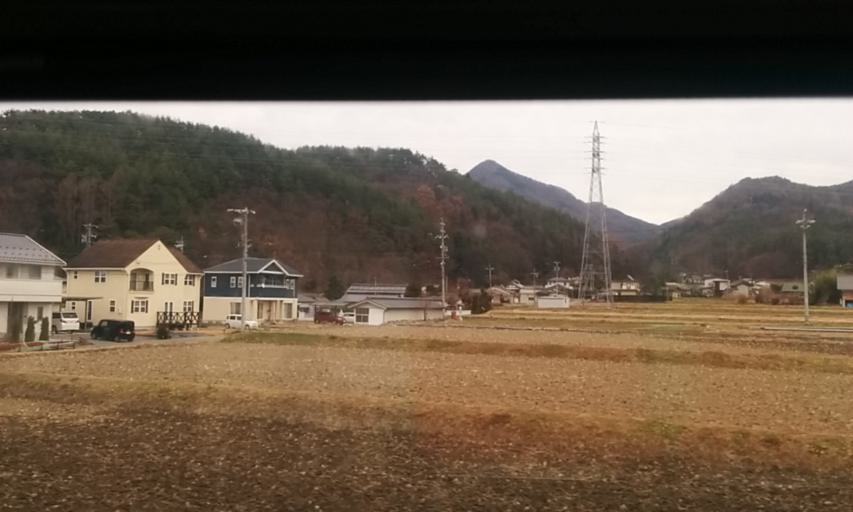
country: JP
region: Nagano
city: Hotaka
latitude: 36.4037
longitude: 138.0144
